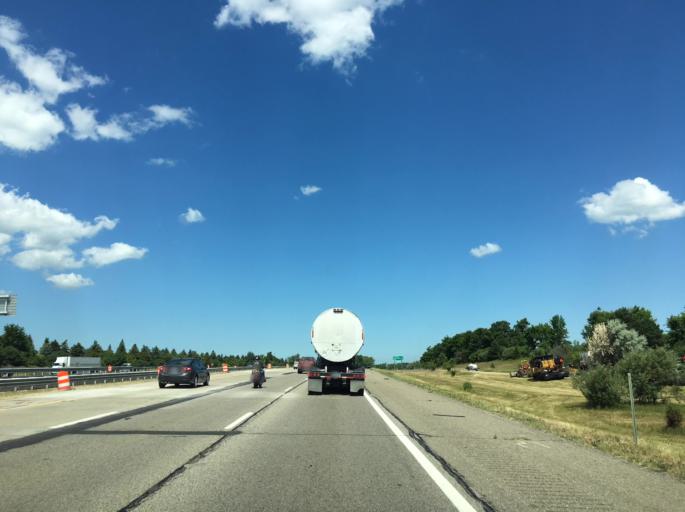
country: US
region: Michigan
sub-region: Oakland County
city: Pontiac
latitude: 42.7080
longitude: -83.3294
